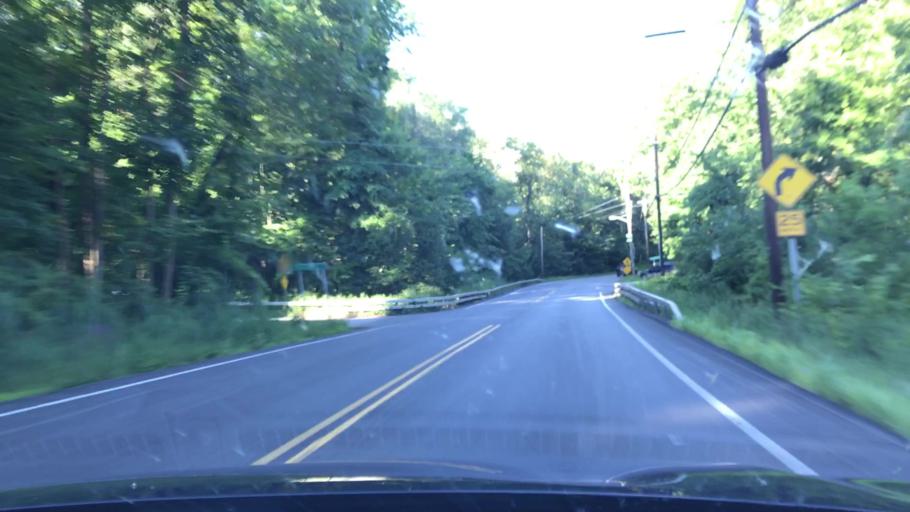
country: US
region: New York
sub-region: Putnam County
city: Mahopac
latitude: 41.3770
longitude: -73.7125
